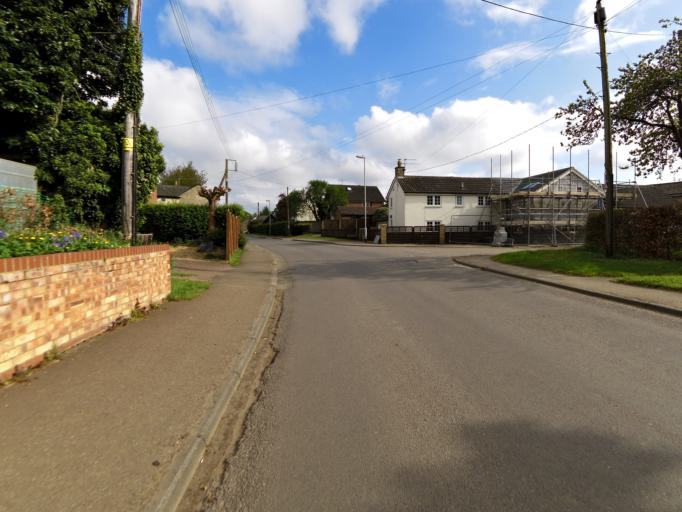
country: GB
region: England
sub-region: Cambridgeshire
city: Bottisham
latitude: 52.2427
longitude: 0.2425
